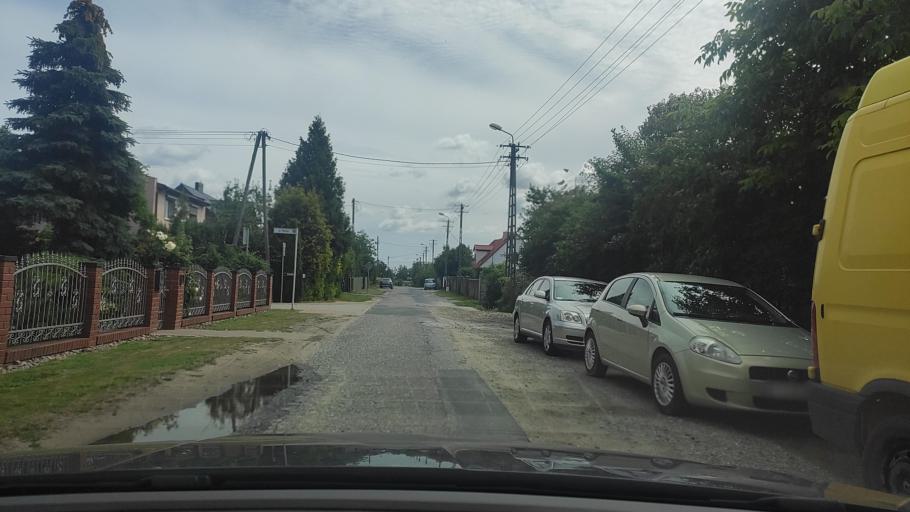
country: PL
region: Greater Poland Voivodeship
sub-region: Powiat poznanski
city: Kostrzyn
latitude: 52.4033
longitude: 17.2087
